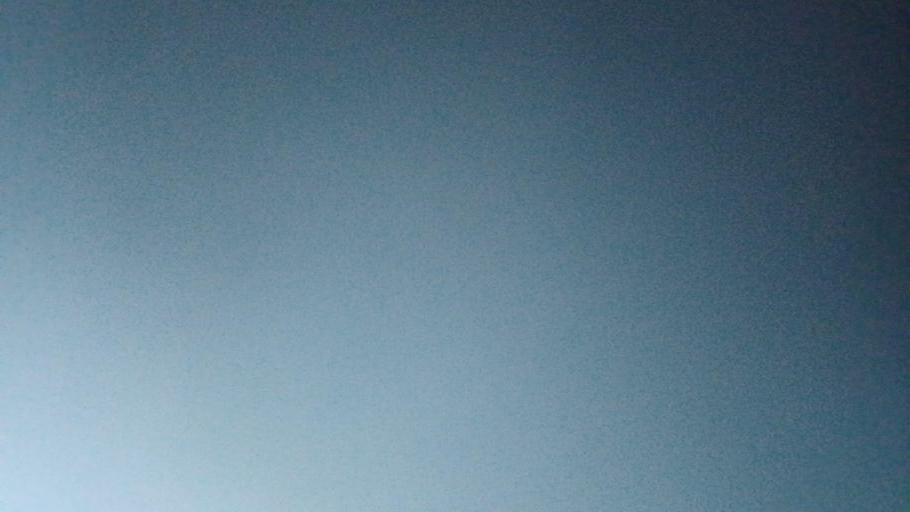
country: ES
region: Catalonia
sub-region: Provincia de Tarragona
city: Camarles
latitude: 40.7757
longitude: 0.6903
